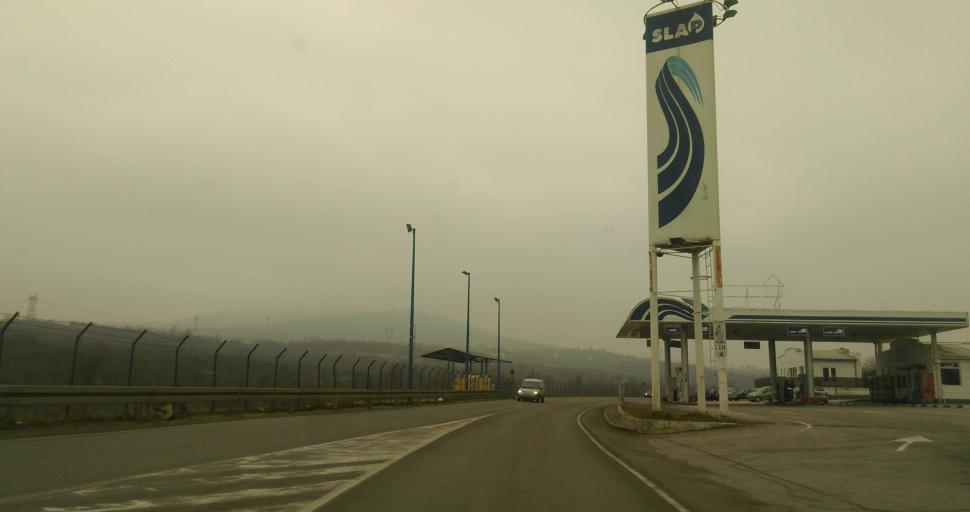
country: RS
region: Central Serbia
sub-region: Belgrade
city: Zvezdara
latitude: 44.7195
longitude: 20.5397
